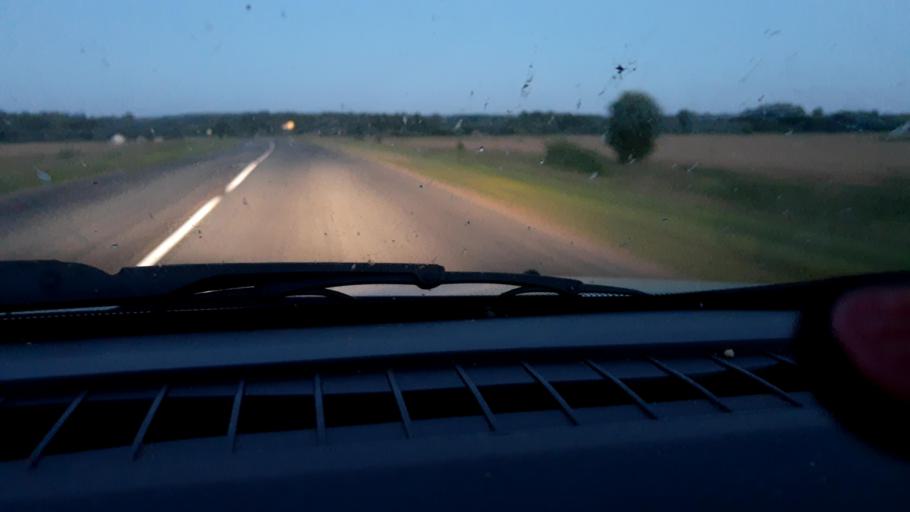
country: RU
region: Nizjnij Novgorod
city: Tonkino
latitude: 57.3563
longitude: 46.4289
